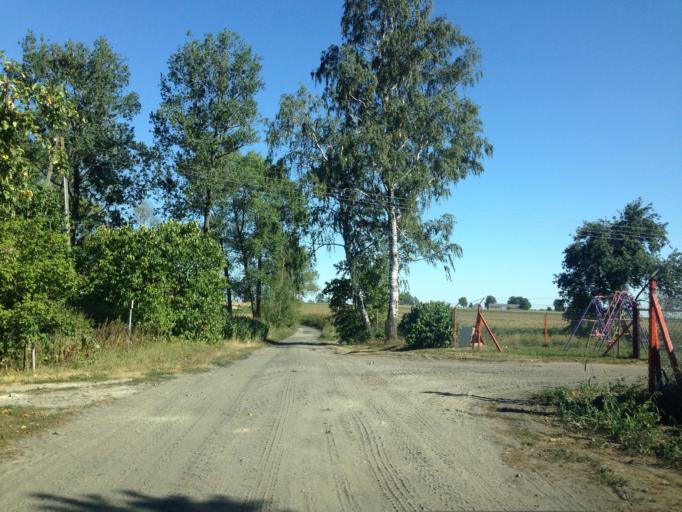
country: PL
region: Kujawsko-Pomorskie
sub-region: Powiat brodnicki
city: Brodnica
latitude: 53.2108
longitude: 19.4175
